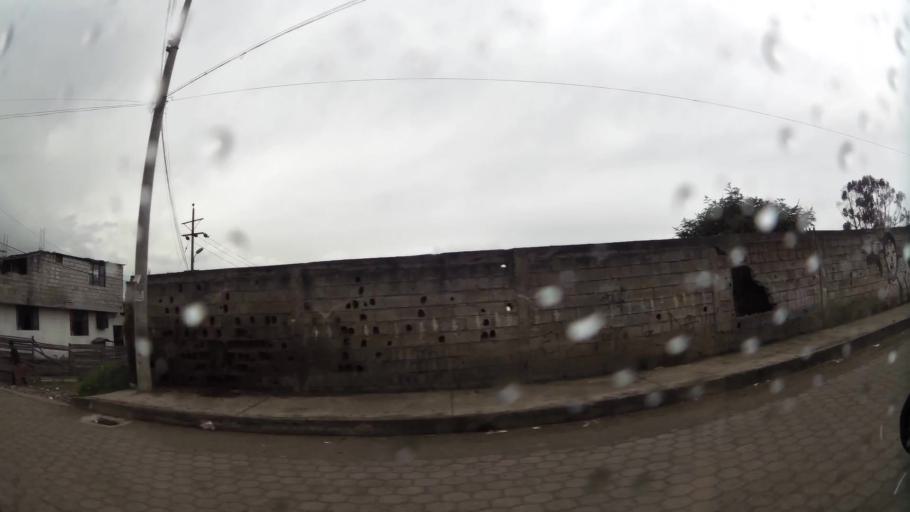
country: EC
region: Pichincha
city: Quito
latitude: -0.3212
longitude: -78.5456
